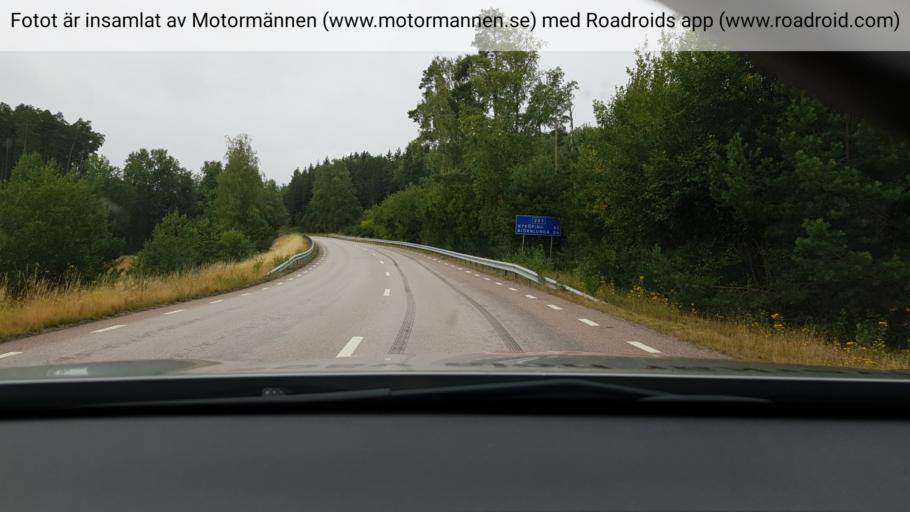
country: SE
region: Soedermanland
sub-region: Strangnas Kommun
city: Mariefred
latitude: 59.2384
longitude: 17.1754
